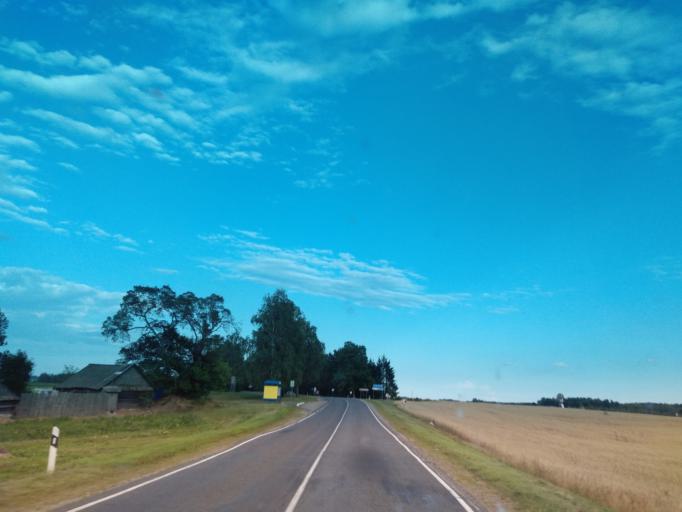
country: BY
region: Minsk
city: Uzda
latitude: 53.4272
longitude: 27.3592
